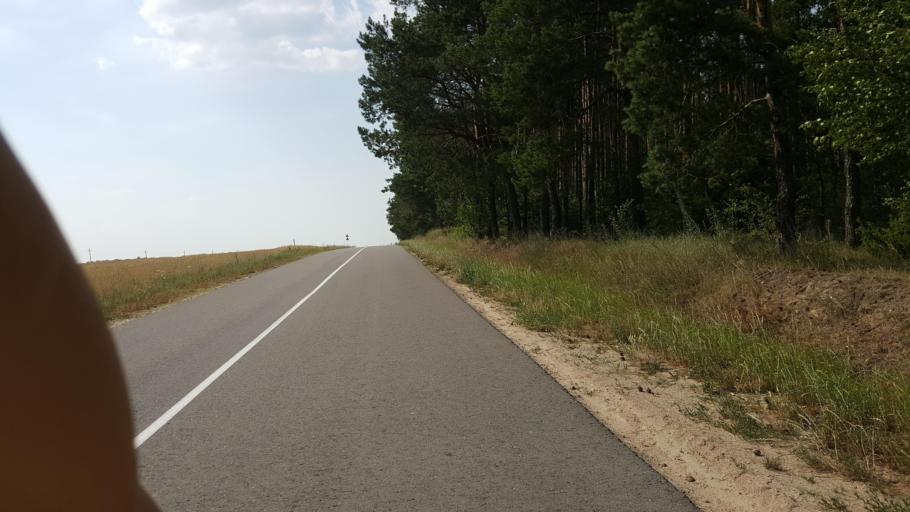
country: BY
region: Brest
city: Kamyanyets
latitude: 52.3644
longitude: 23.8094
